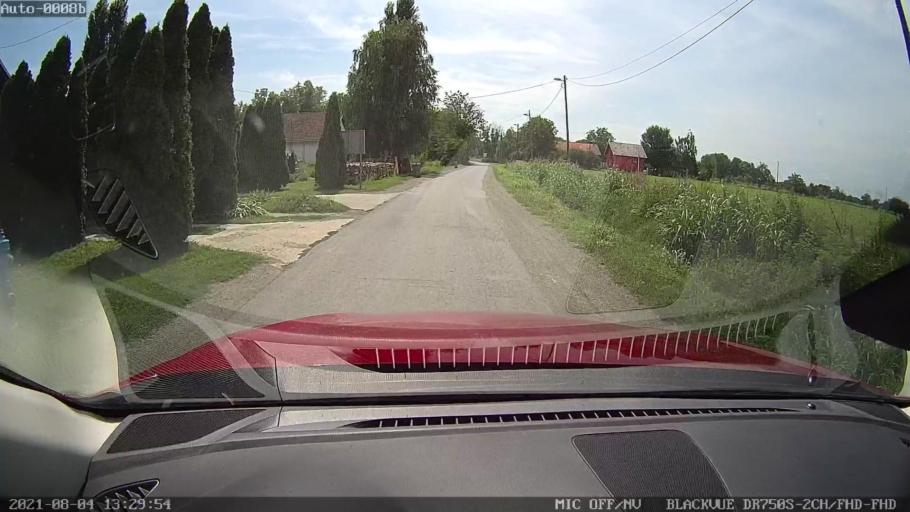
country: HR
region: Osjecko-Baranjska
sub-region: Grad Osijek
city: Bilje
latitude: 45.6025
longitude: 18.7829
